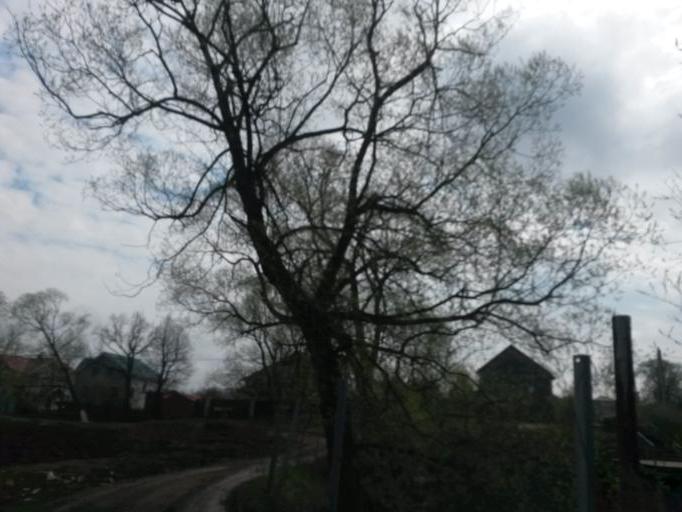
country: RU
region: Moskovskaya
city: Lyubuchany
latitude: 55.2573
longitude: 37.6025
